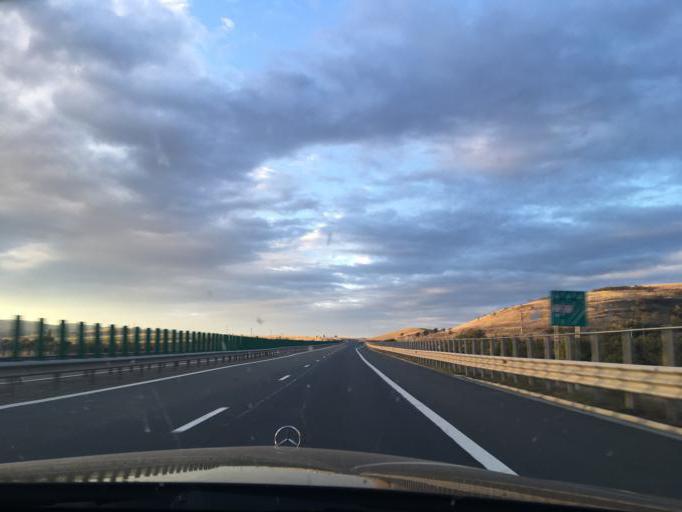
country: RO
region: Cluj
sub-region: Comuna Sandulesti
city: Copaceni
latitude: 46.5777
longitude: 23.7420
